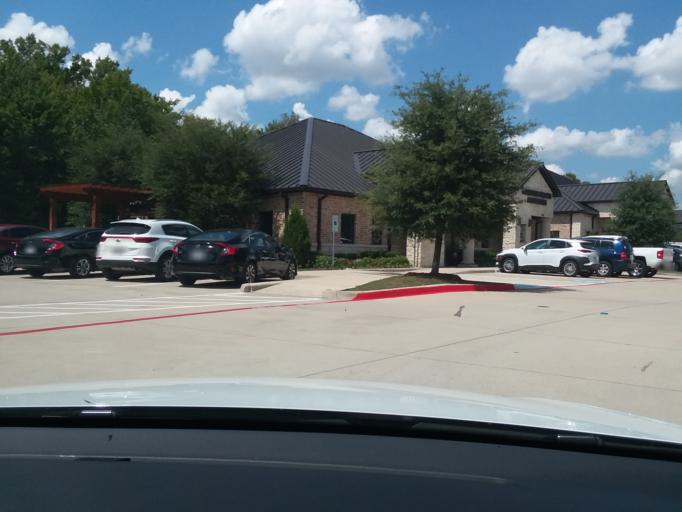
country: US
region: Texas
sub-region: Collin County
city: McKinney
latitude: 33.2171
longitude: -96.6849
